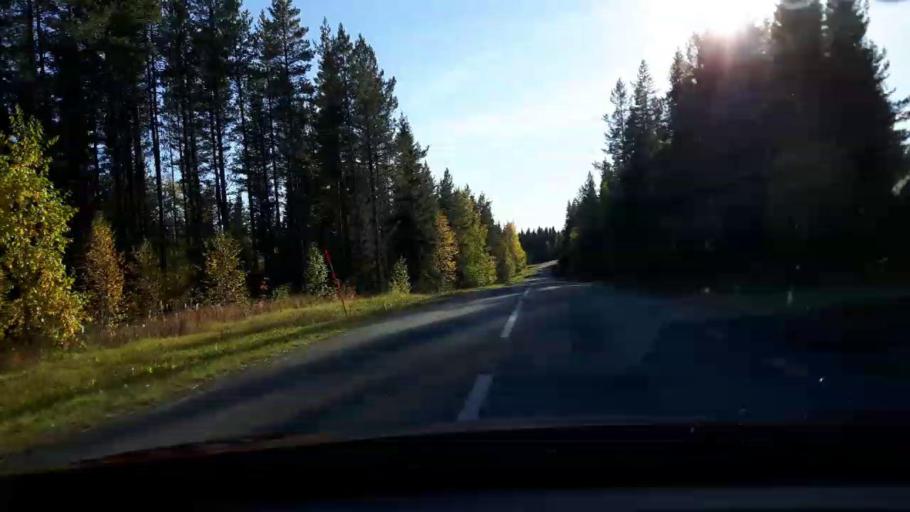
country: SE
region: Jaemtland
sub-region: OEstersunds Kommun
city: Lit
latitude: 63.8300
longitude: 14.8718
